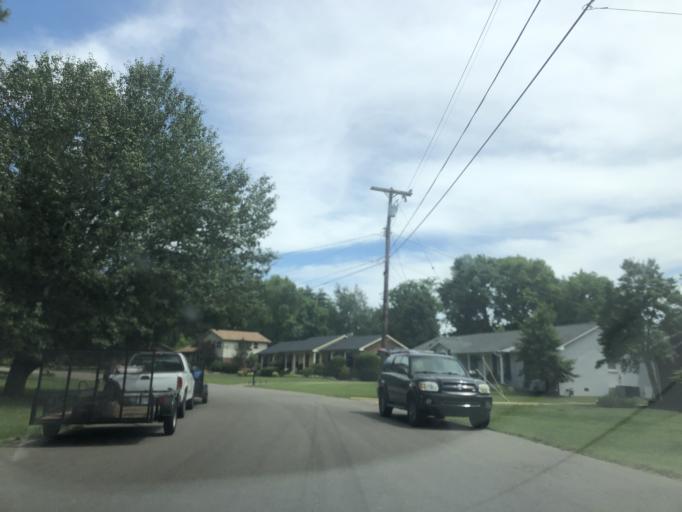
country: US
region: Tennessee
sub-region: Davidson County
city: Belle Meade
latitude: 36.0787
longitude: -86.9394
